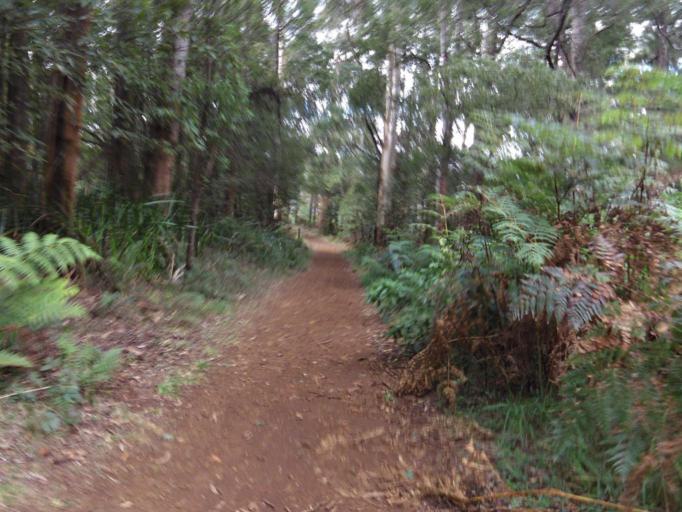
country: AU
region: Victoria
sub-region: Yarra Ranges
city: Olinda
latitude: -37.8537
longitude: 145.3789
